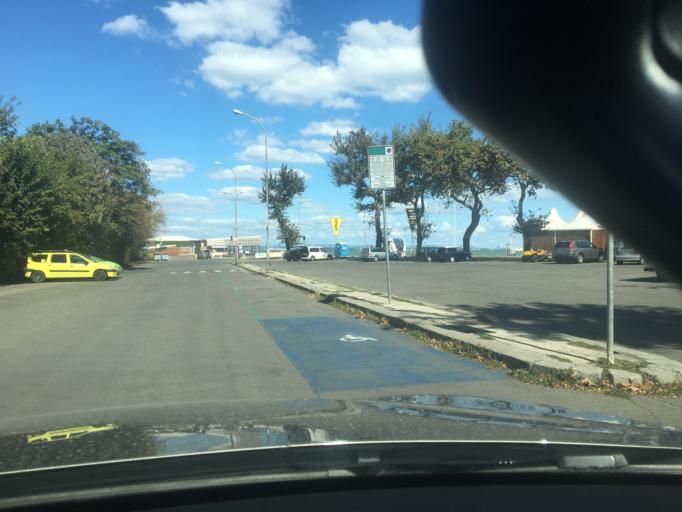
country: BG
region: Burgas
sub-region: Obshtina Burgas
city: Burgas
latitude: 42.5089
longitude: 27.4834
